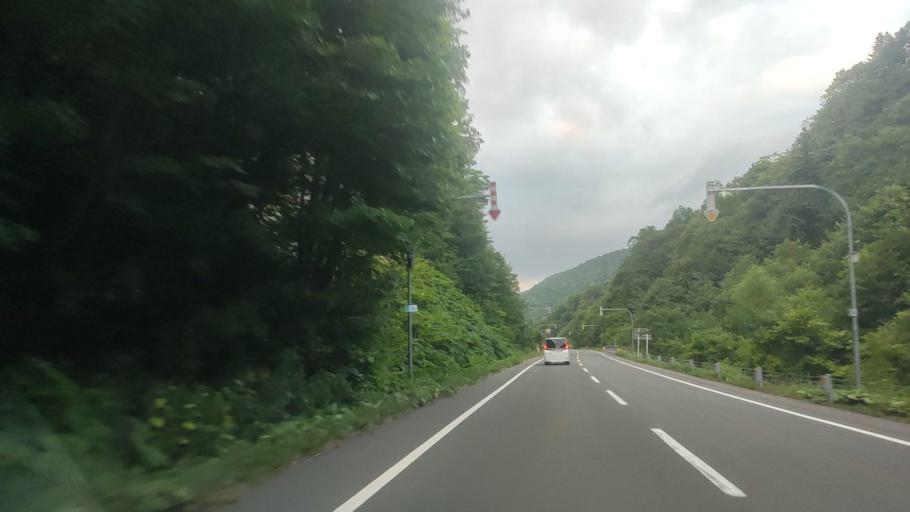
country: JP
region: Hokkaido
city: Shimo-furano
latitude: 43.3421
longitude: 142.2789
